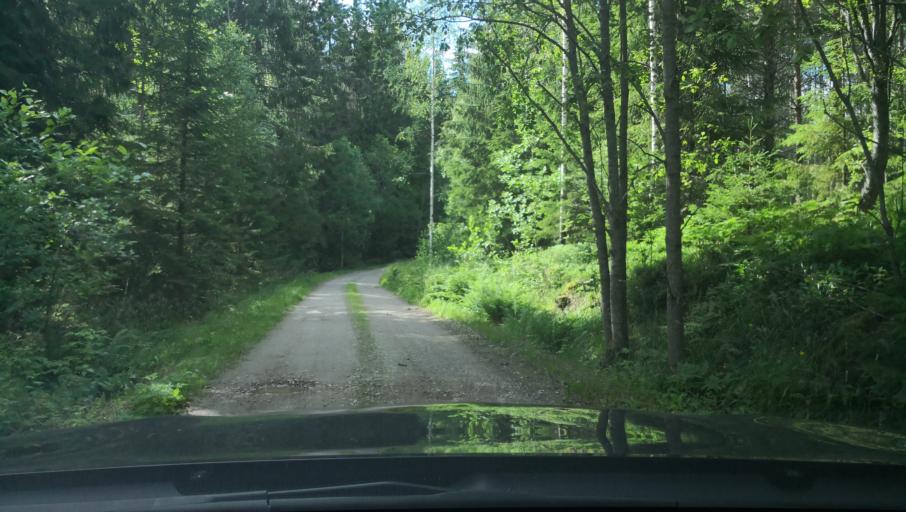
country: SE
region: Vaestmanland
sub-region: Kopings Kommun
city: Koping
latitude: 59.6405
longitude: 16.0657
